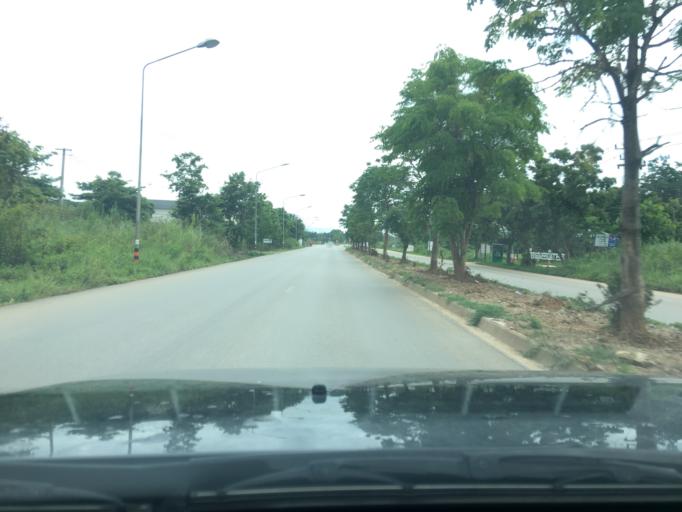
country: TH
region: Chiang Rai
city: Chiang Rai
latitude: 19.9566
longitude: 99.8646
